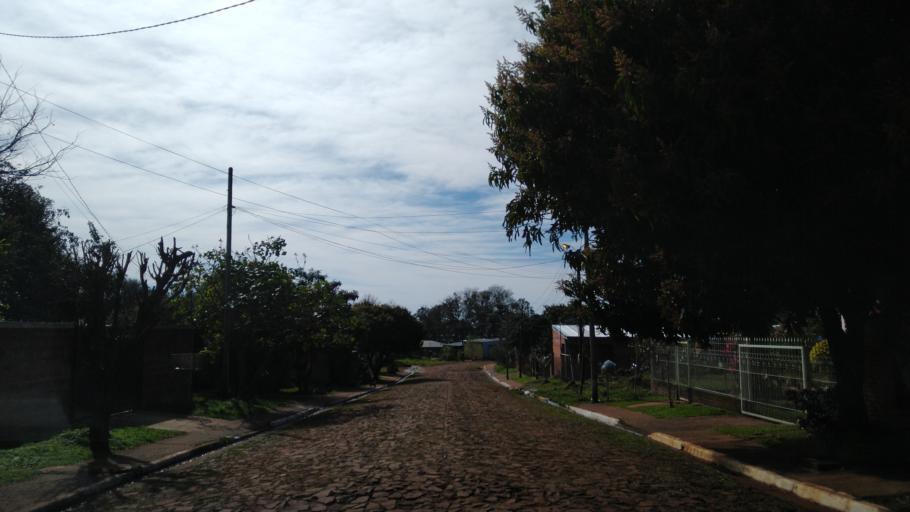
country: AR
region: Misiones
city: Garupa
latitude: -27.4591
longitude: -55.8580
